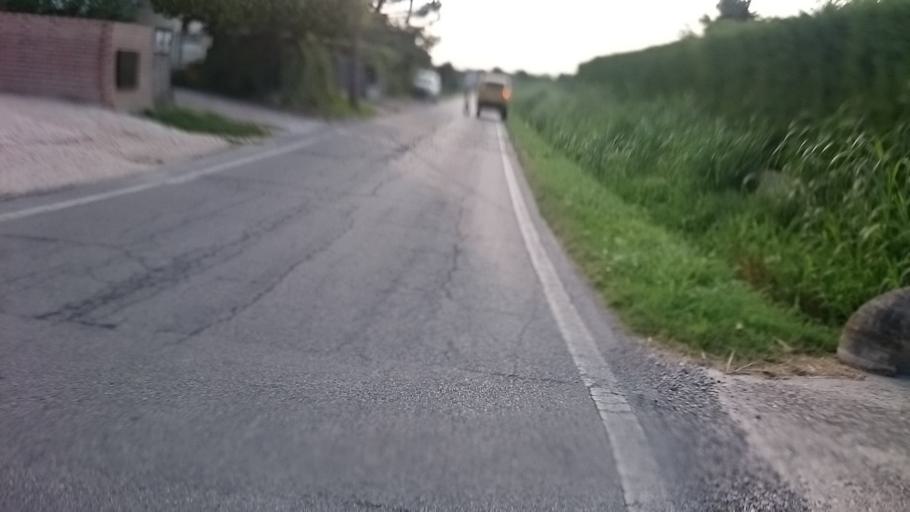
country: IT
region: Veneto
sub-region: Provincia di Padova
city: Villatora
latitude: 45.3706
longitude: 11.9621
